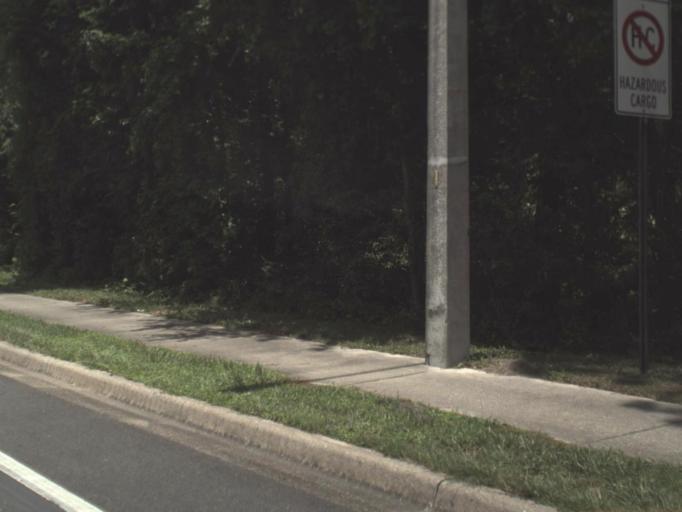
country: US
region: Florida
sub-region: Alachua County
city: Gainesville
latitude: 29.6884
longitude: -82.3046
